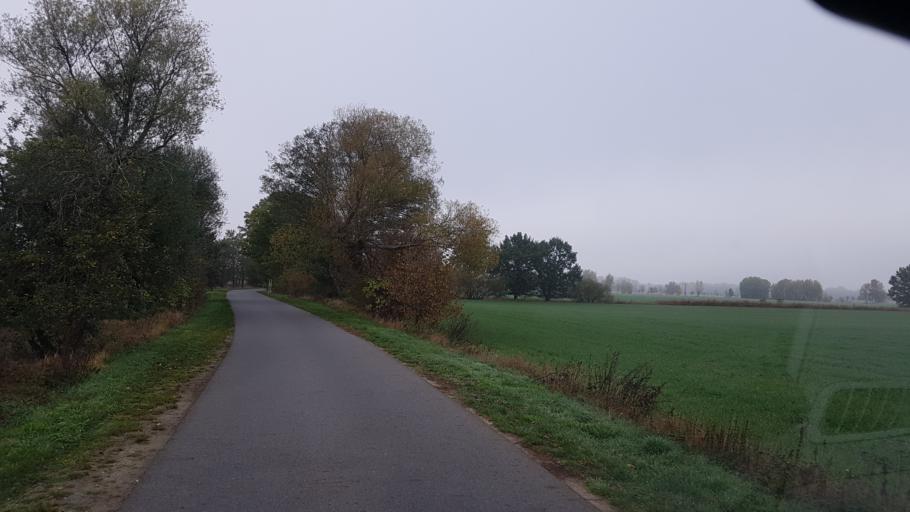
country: DE
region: Brandenburg
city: Schonewalde
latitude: 51.6782
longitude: 13.6182
